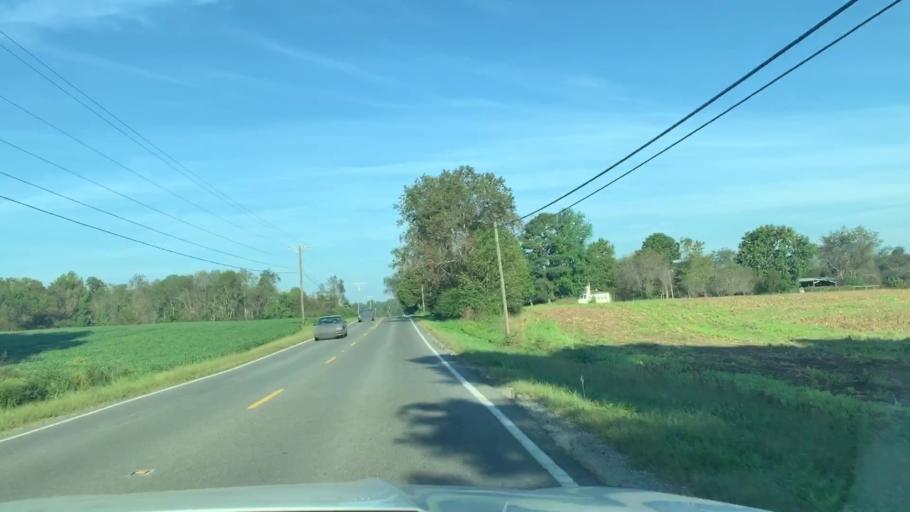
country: US
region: Virginia
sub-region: Lancaster County
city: Lancaster
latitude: 37.7657
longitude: -76.4285
